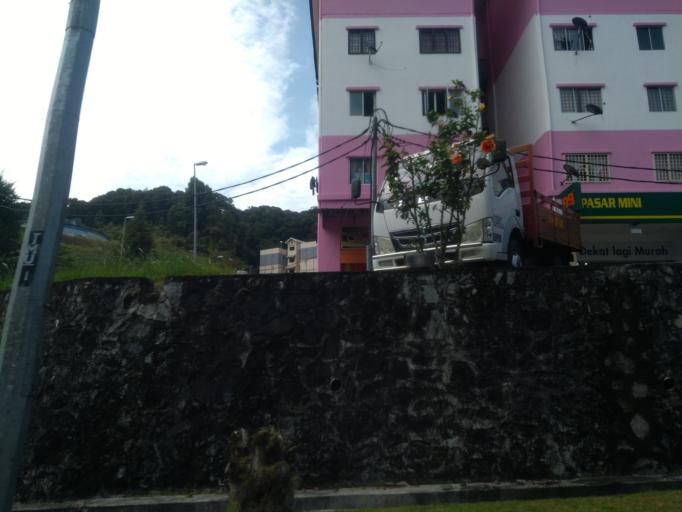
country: MY
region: Pahang
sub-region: Cameron Highlands
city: Tanah Rata
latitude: 4.4684
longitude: 101.3737
